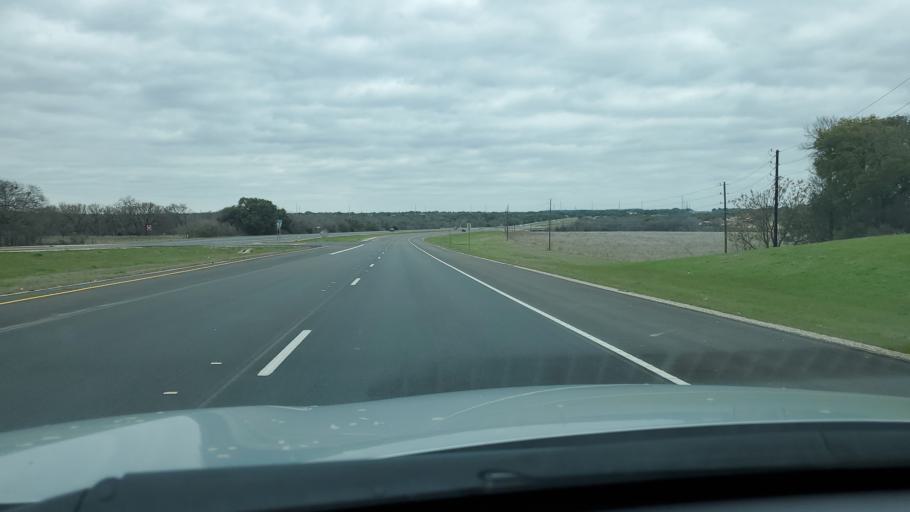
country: US
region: Texas
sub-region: Williamson County
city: Florence
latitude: 30.9664
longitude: -97.7798
